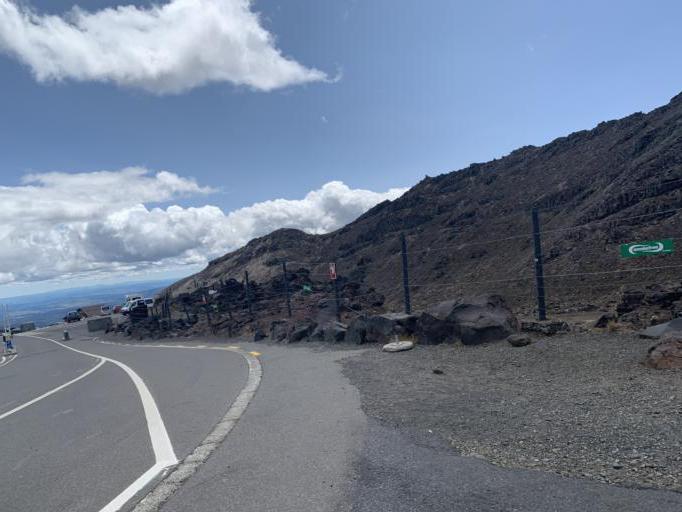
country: NZ
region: Manawatu-Wanganui
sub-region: Ruapehu District
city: Waiouru
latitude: -39.2369
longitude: 175.5565
